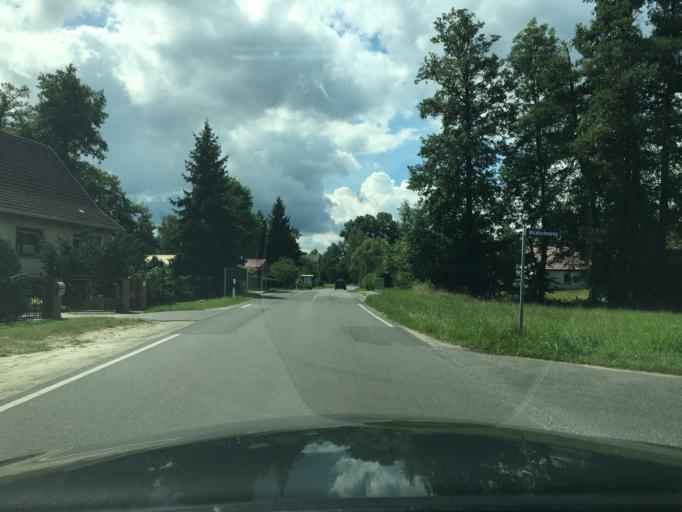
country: DE
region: Brandenburg
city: Burg
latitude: 51.8493
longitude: 14.1033
